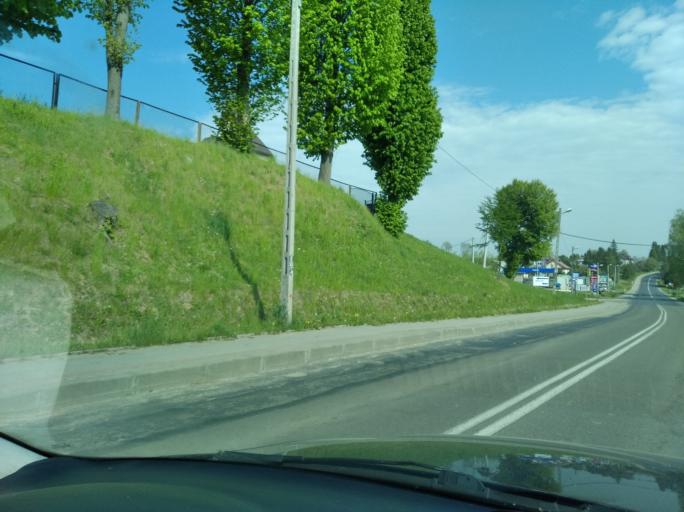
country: PL
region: Subcarpathian Voivodeship
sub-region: Powiat rzeszowski
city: Dynow
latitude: 49.8230
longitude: 22.2344
